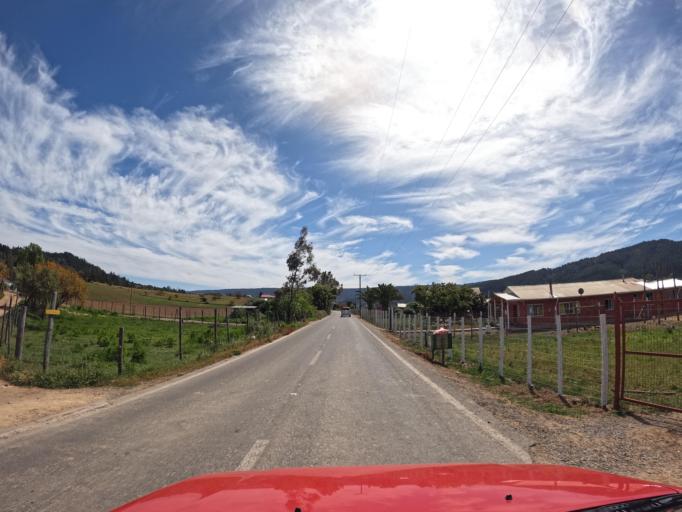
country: CL
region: Maule
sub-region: Provincia de Talca
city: Constitucion
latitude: -34.9916
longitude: -71.9984
